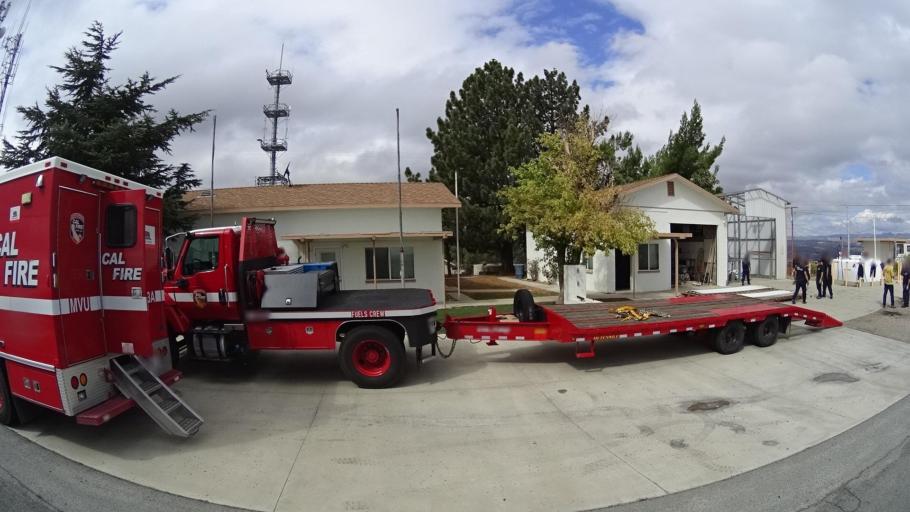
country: US
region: California
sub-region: San Diego County
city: Campo
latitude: 32.6475
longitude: -116.3172
